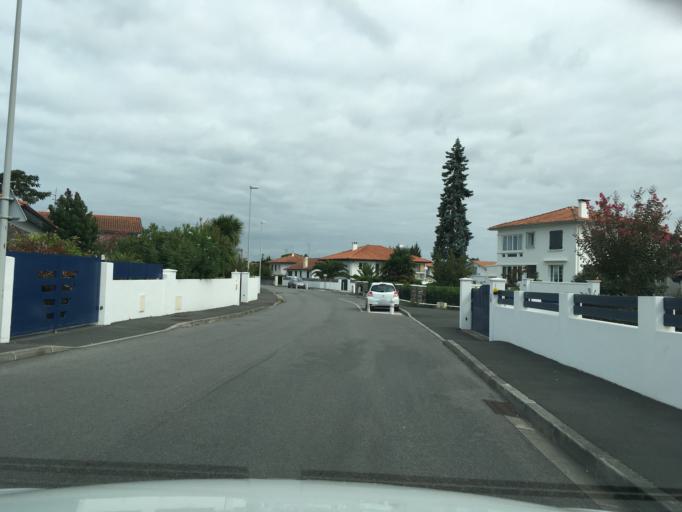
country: FR
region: Aquitaine
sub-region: Departement des Pyrenees-Atlantiques
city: Anglet
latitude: 43.4889
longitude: -1.5169
